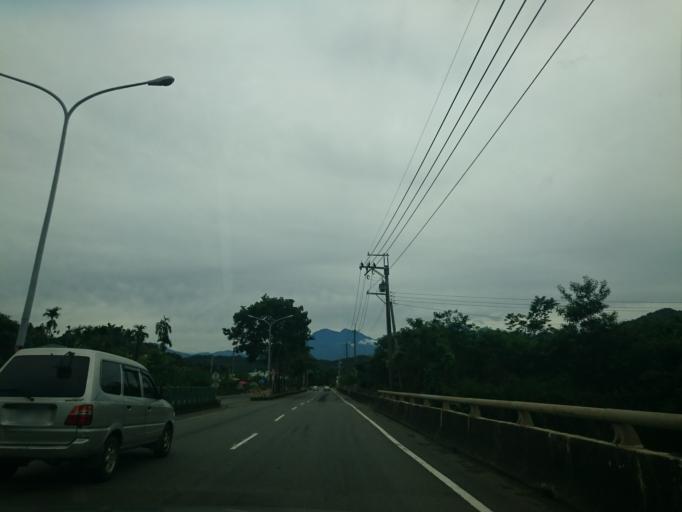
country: TW
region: Taiwan
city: Lugu
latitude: 23.8331
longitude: 120.7357
